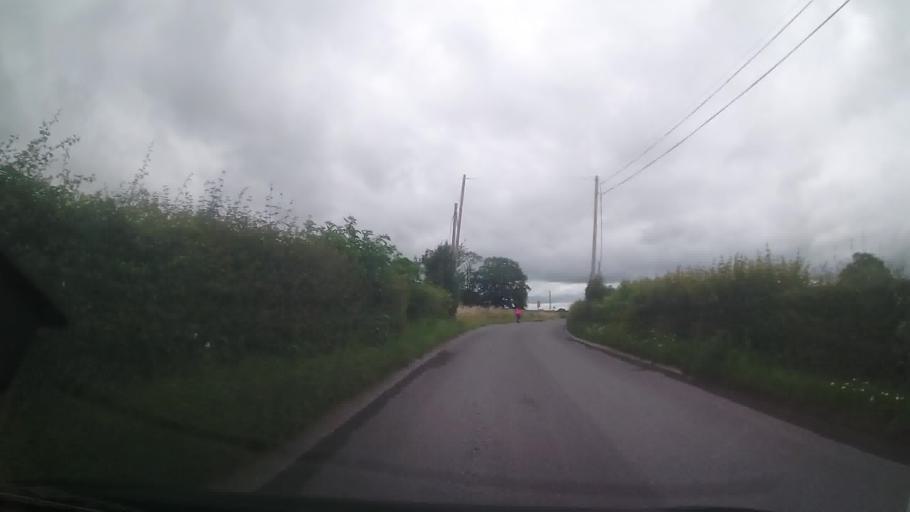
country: GB
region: England
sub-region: Shropshire
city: Petton
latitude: 52.8373
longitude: -2.8163
